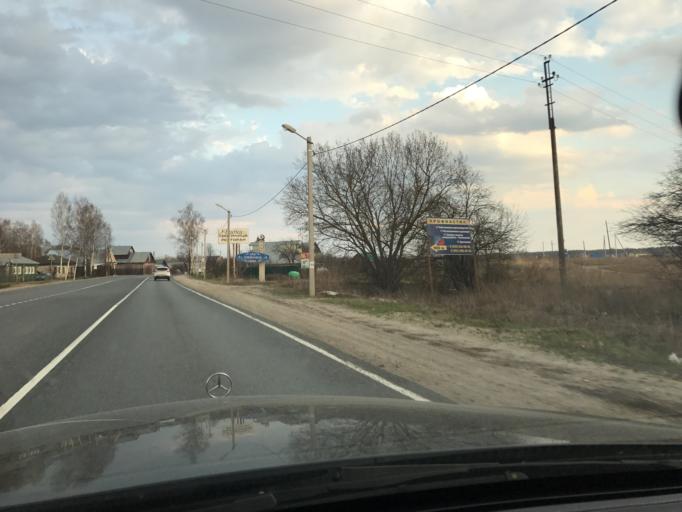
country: RU
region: Vladimir
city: Murom
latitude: 55.6163
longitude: 41.9425
